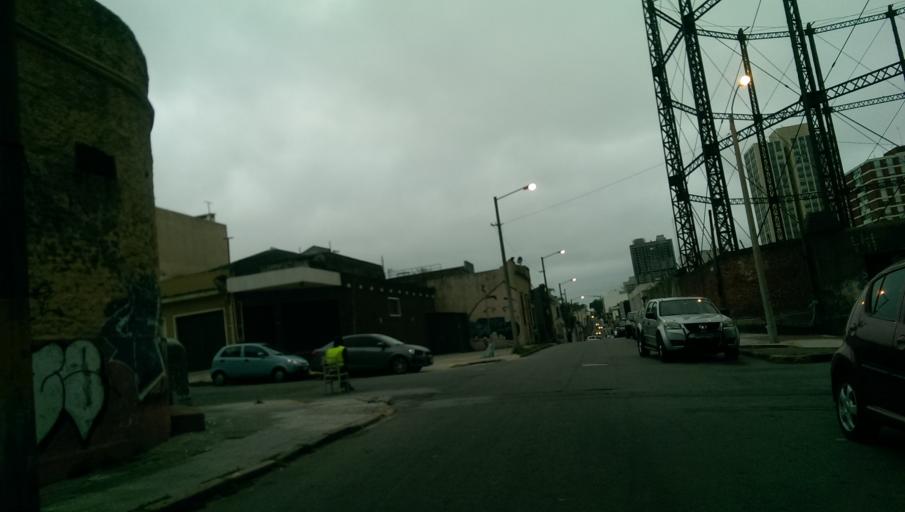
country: UY
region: Montevideo
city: Montevideo
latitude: -34.9117
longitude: -56.1944
